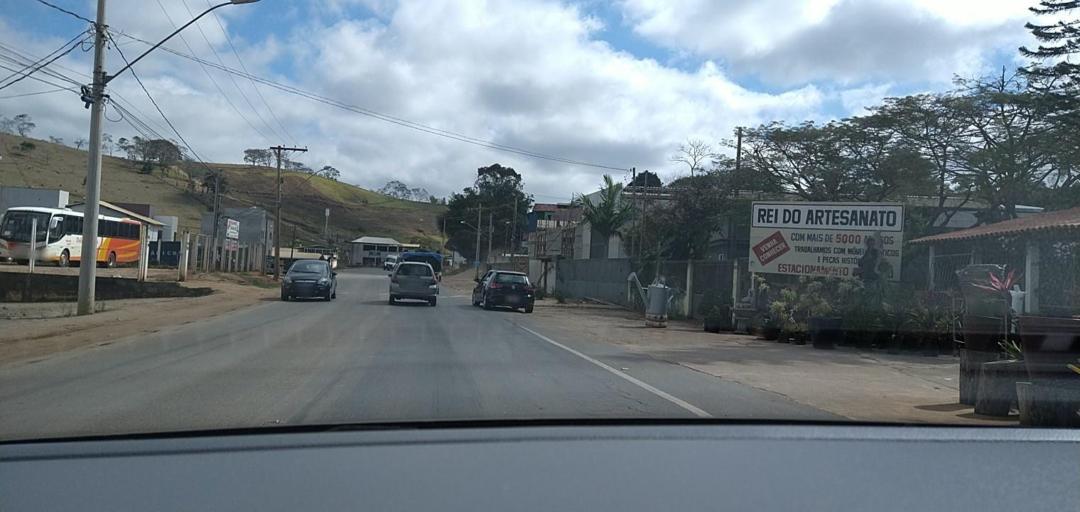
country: BR
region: Minas Gerais
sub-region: Vicosa
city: Vicosa
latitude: -20.6657
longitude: -42.8557
